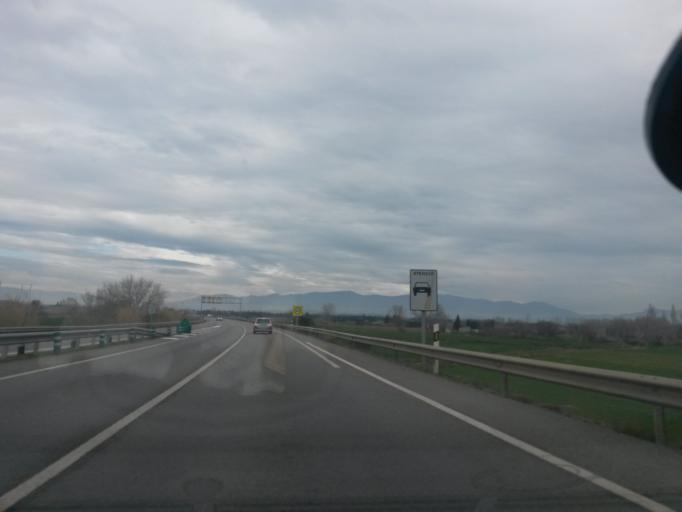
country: ES
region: Catalonia
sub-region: Provincia de Girona
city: Vilabertran
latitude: 42.2698
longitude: 2.9880
